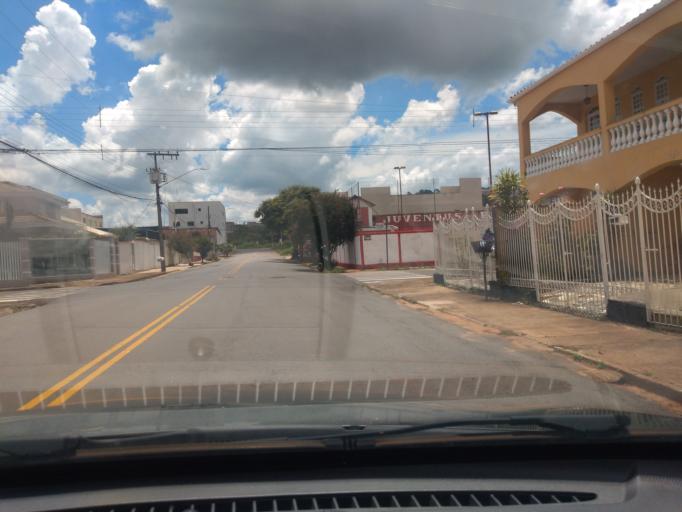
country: BR
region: Minas Gerais
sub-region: Tres Coracoes
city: Tres Coracoes
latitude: -21.6747
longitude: -45.2683
